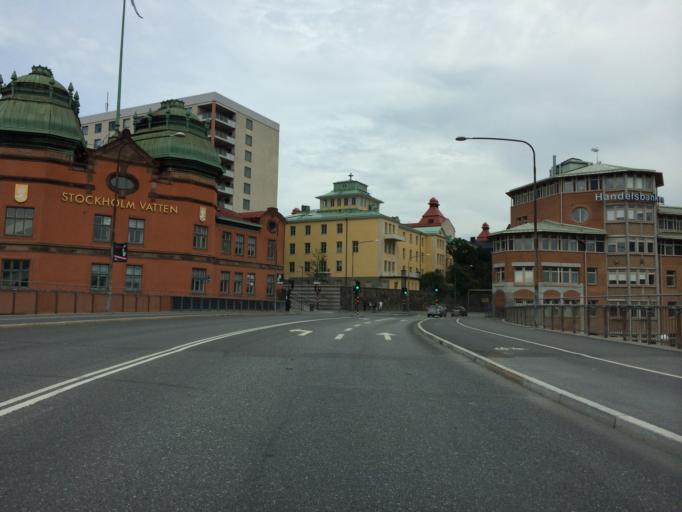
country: SE
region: Stockholm
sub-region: Stockholms Kommun
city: Stockholm
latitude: 59.3360
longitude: 18.0474
